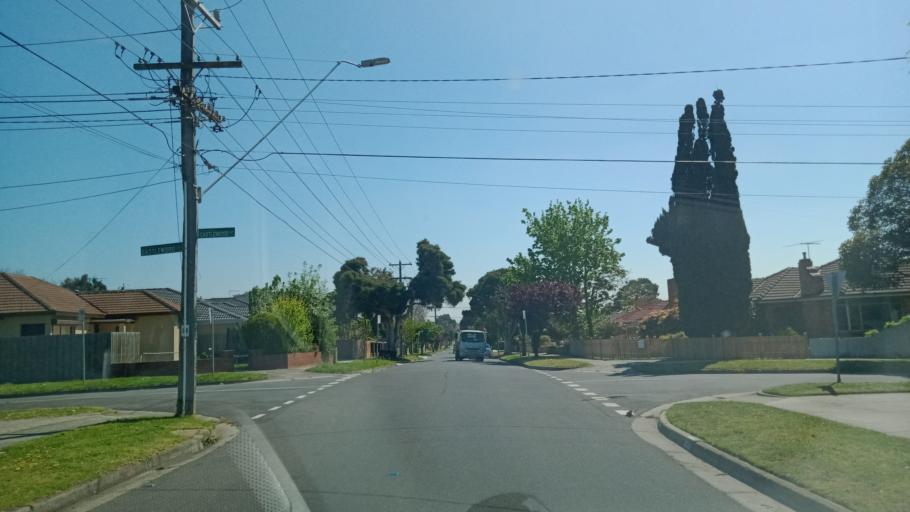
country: AU
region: Victoria
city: Murrumbeena
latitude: -37.9161
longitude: 145.0672
